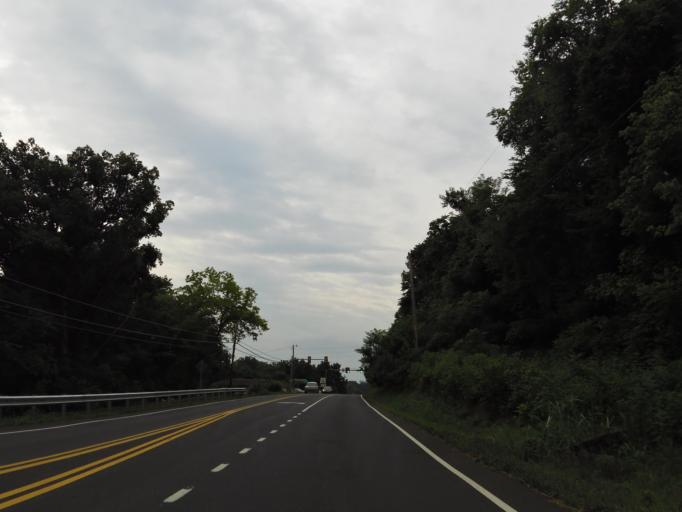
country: US
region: Tennessee
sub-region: Blount County
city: Eagleton Village
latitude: 35.8253
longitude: -83.9399
